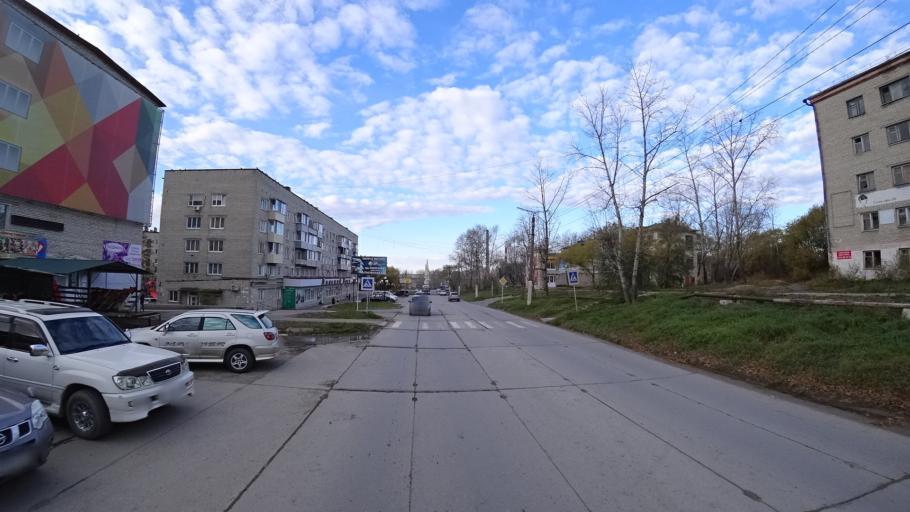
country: RU
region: Khabarovsk Krai
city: Amursk
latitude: 50.2310
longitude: 136.9040
